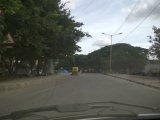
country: IN
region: Karnataka
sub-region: Bangalore Urban
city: Bangalore
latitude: 12.9963
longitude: 77.5506
